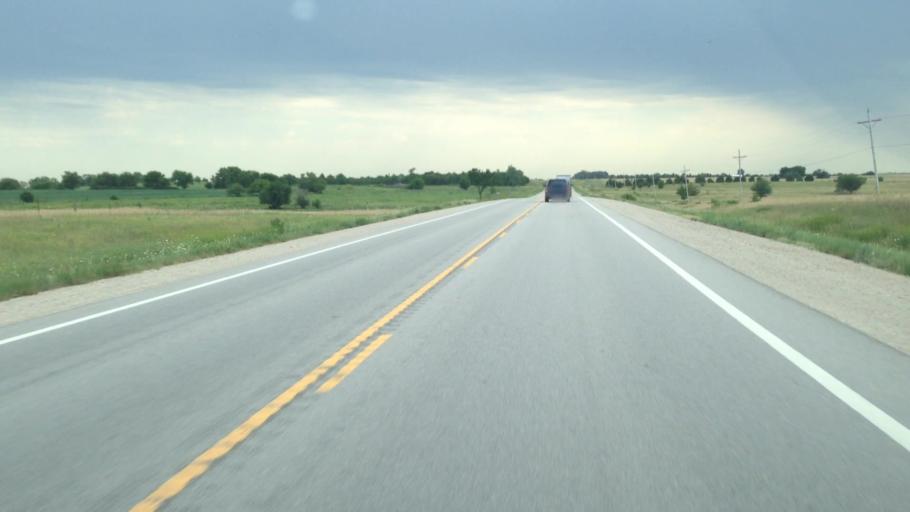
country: US
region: Kansas
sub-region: Coffey County
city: Burlington
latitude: 38.3315
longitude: -95.7290
